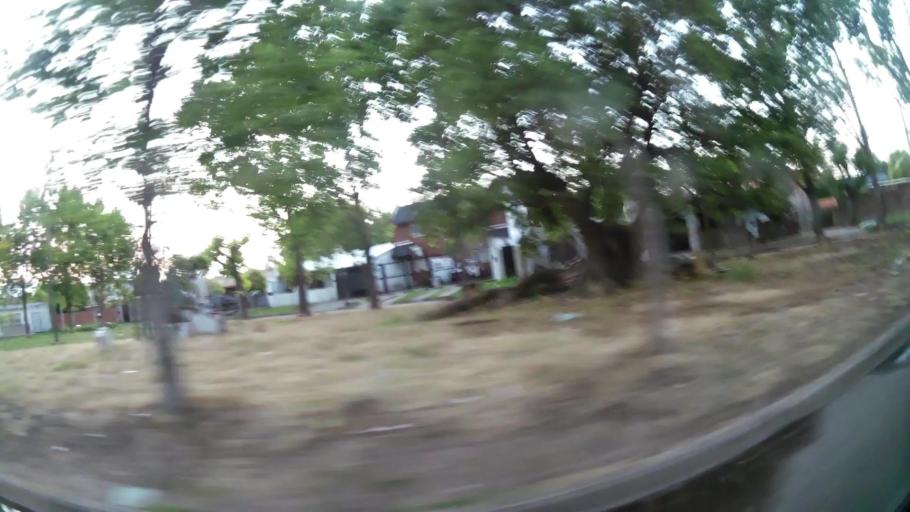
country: AR
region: Buenos Aires
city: San Nicolas de los Arroyos
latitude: -33.3476
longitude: -60.1943
